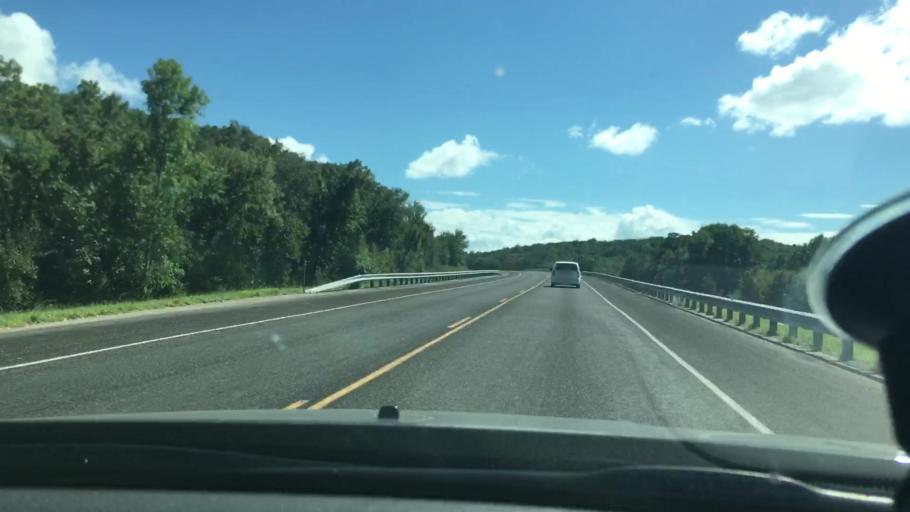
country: US
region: Oklahoma
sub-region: Sequoyah County
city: Vian
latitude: 35.5300
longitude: -94.9734
